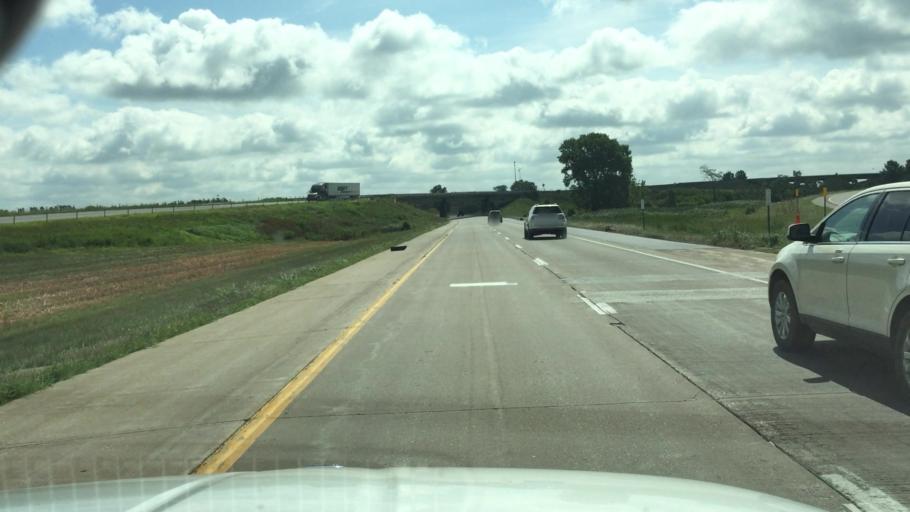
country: US
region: Iowa
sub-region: Scott County
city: Walcott
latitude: 41.6033
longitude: -90.6813
